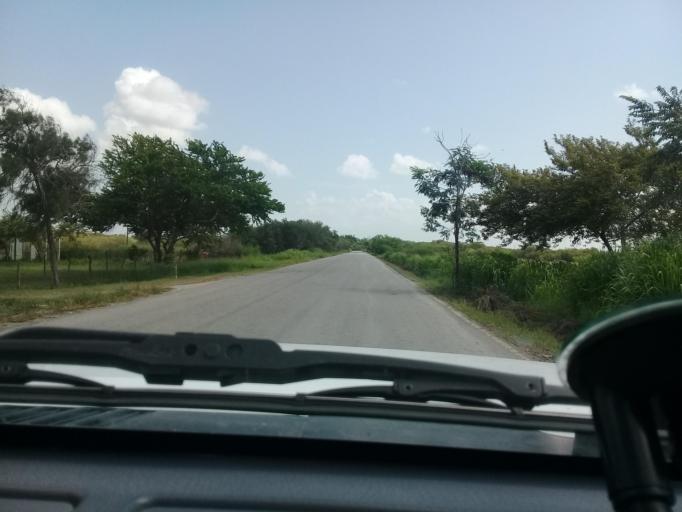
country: MX
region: Veracruz
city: Moralillo
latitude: 22.1840
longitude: -97.9465
